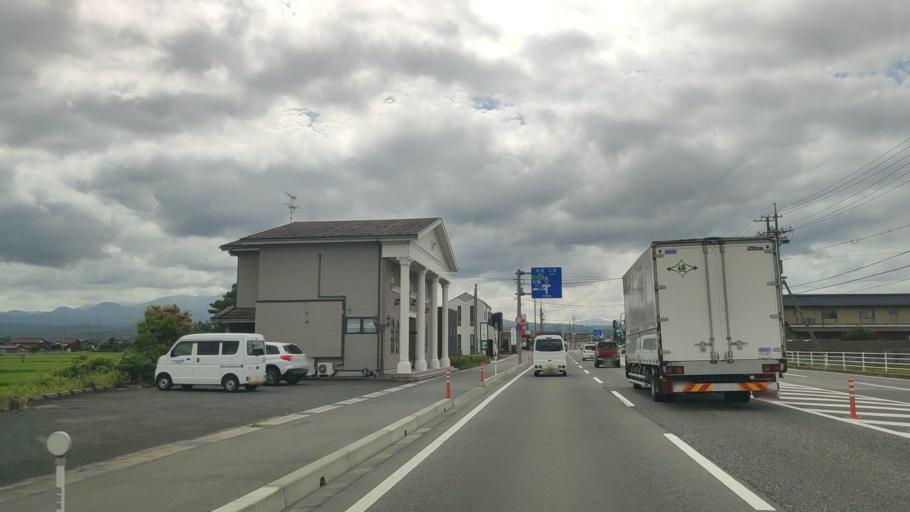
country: JP
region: Tottori
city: Yonago
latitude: 35.3992
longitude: 133.3770
